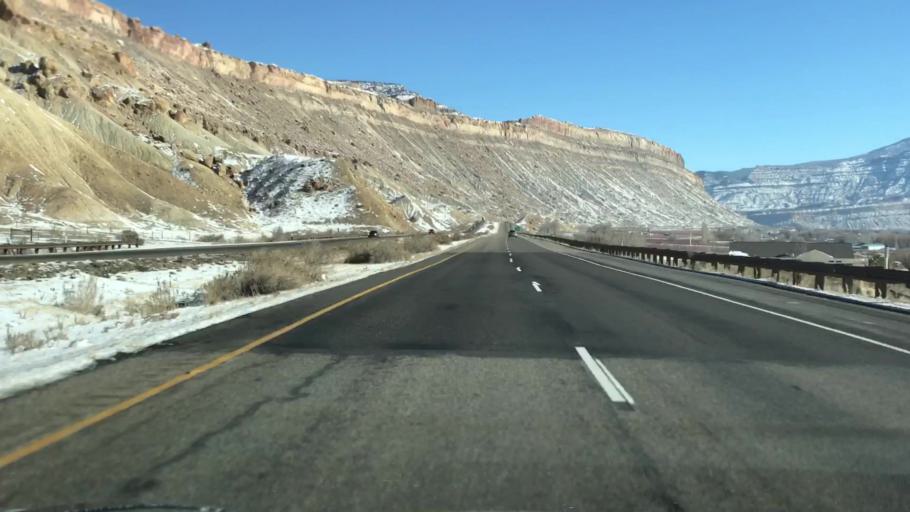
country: US
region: Colorado
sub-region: Mesa County
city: Palisade
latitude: 39.1175
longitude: -108.3896
